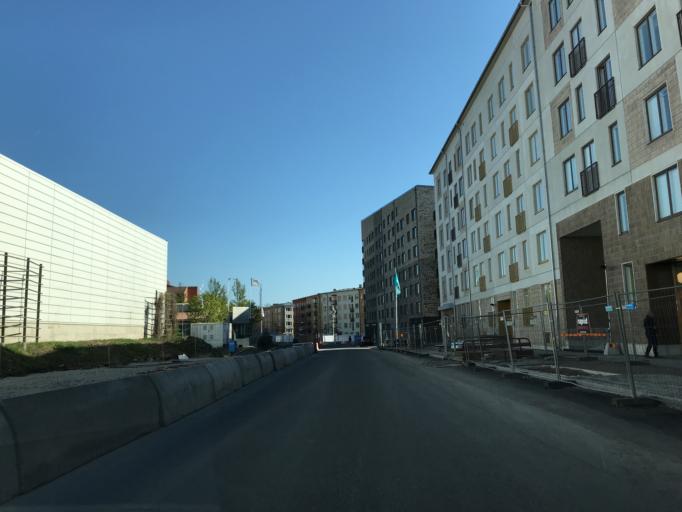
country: SE
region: Stockholm
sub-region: Huddinge Kommun
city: Huddinge
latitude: 59.2816
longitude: 18.0036
